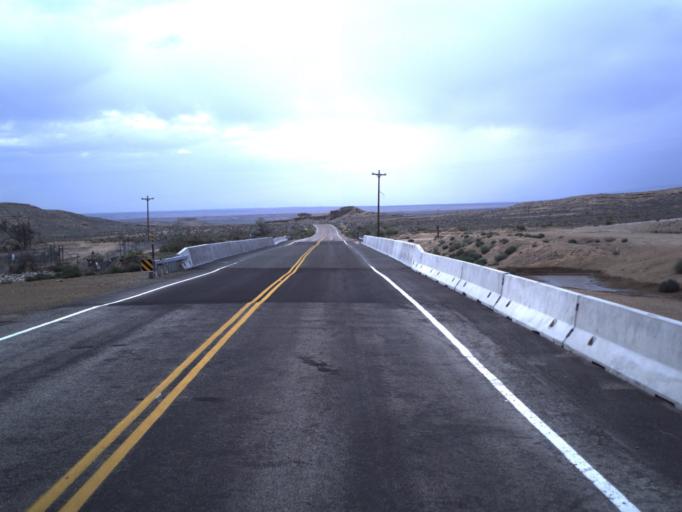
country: US
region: Colorado
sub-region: Rio Blanco County
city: Rangely
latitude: 40.0194
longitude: -109.1731
